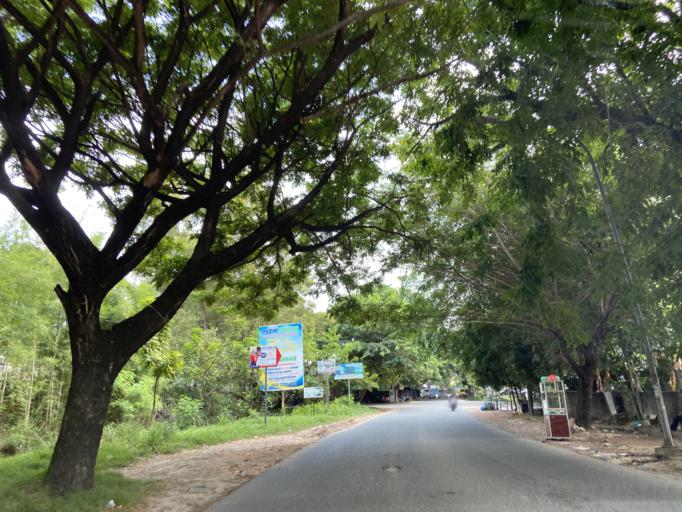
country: SG
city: Singapore
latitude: 1.1312
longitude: 104.0343
